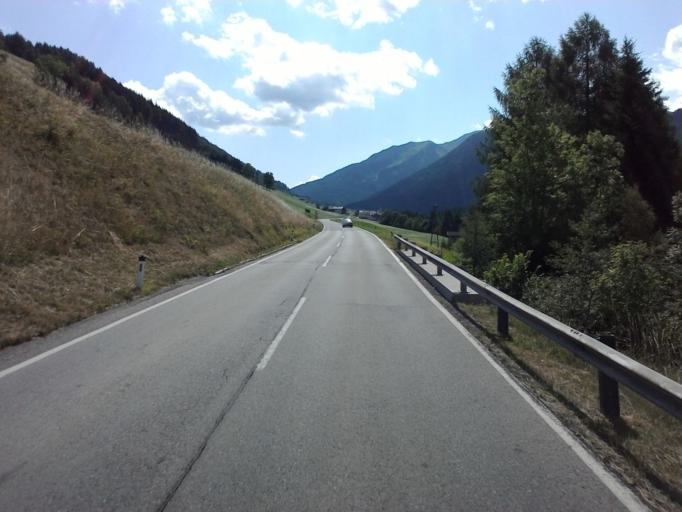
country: AT
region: Tyrol
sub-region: Politischer Bezirk Lienz
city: Strassen
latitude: 46.7361
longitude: 12.4772
